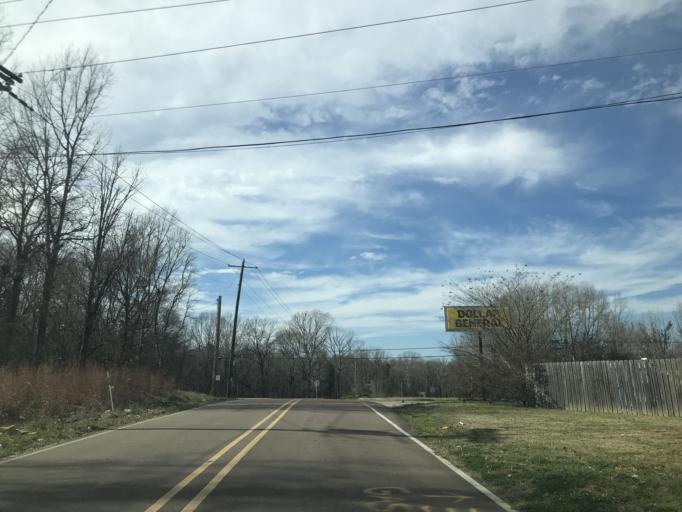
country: US
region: Mississippi
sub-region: Hinds County
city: Edwards
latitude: 32.1113
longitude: -90.6054
